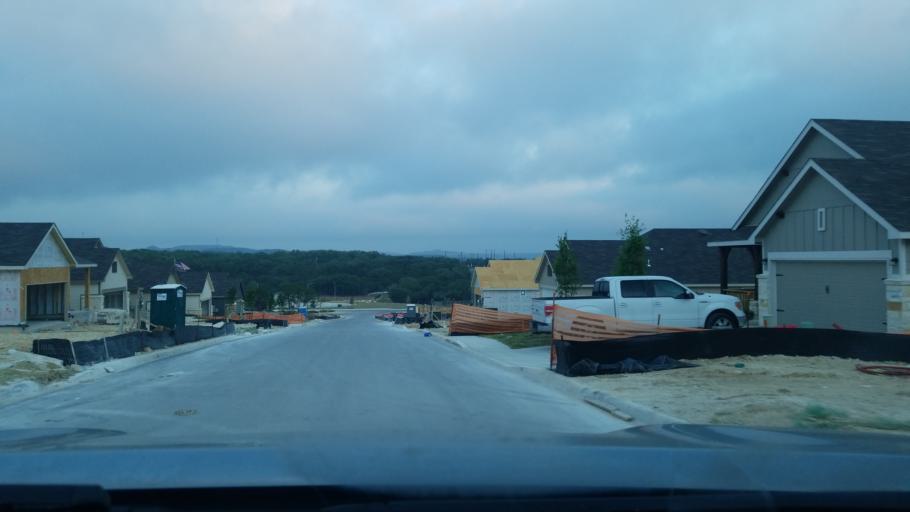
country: US
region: Texas
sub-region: Bexar County
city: Timberwood Park
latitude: 29.7076
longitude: -98.5028
